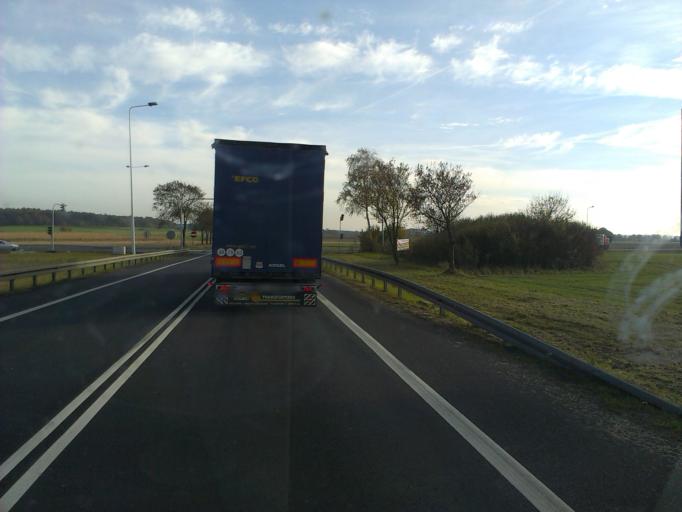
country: PL
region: Lower Silesian Voivodeship
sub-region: Powiat polkowicki
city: Radwanice
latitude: 51.5994
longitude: 15.9607
